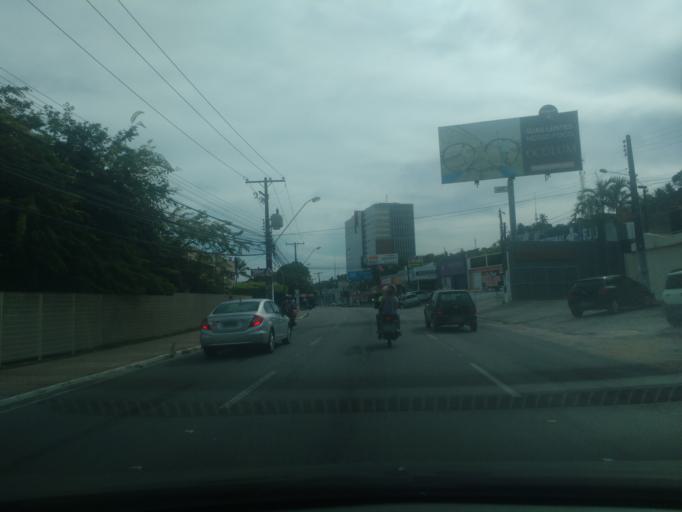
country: BR
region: Alagoas
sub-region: Maceio
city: Maceio
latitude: -9.6471
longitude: -35.7155
